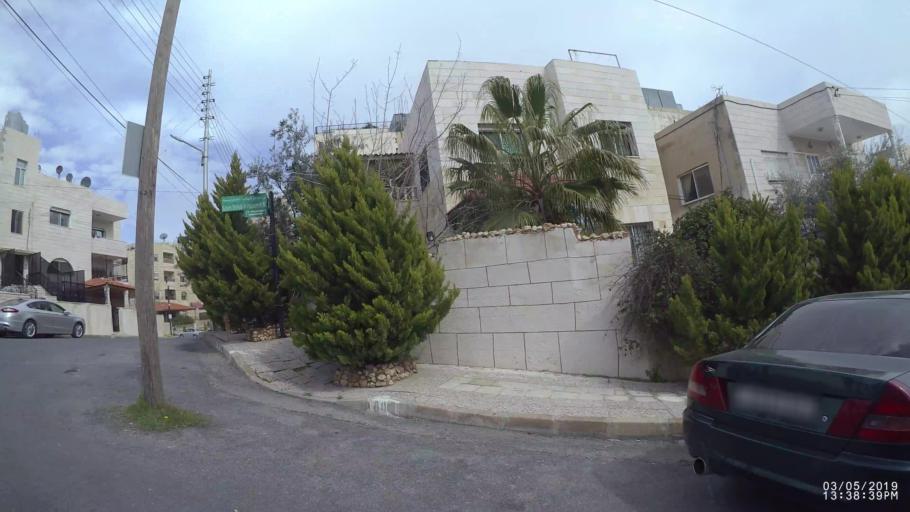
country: JO
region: Amman
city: Amman
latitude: 31.9991
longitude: 35.9404
